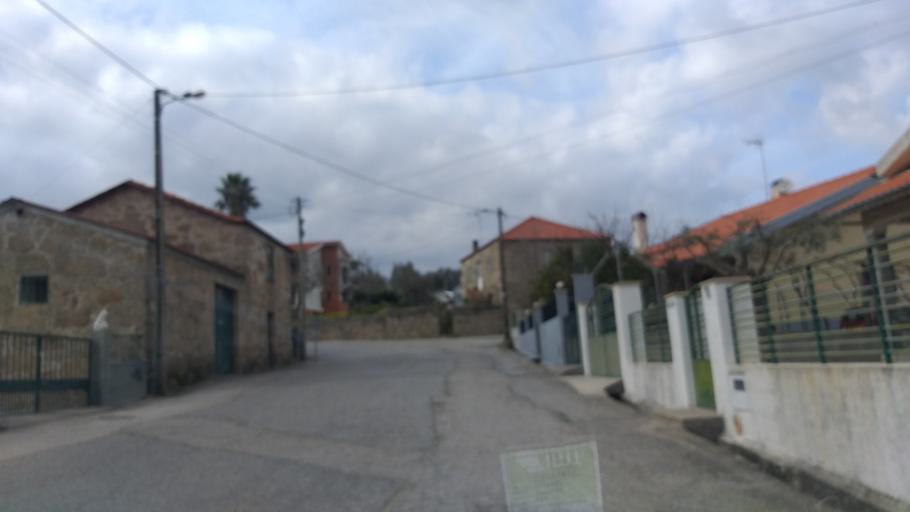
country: PT
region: Guarda
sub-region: Seia
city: Seia
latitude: 40.4495
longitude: -7.7110
